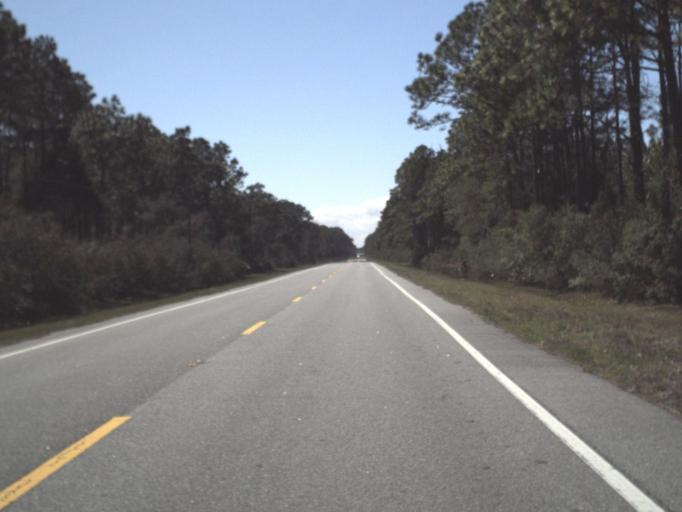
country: US
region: Florida
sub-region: Franklin County
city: Carrabelle
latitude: 29.9232
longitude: -84.4865
